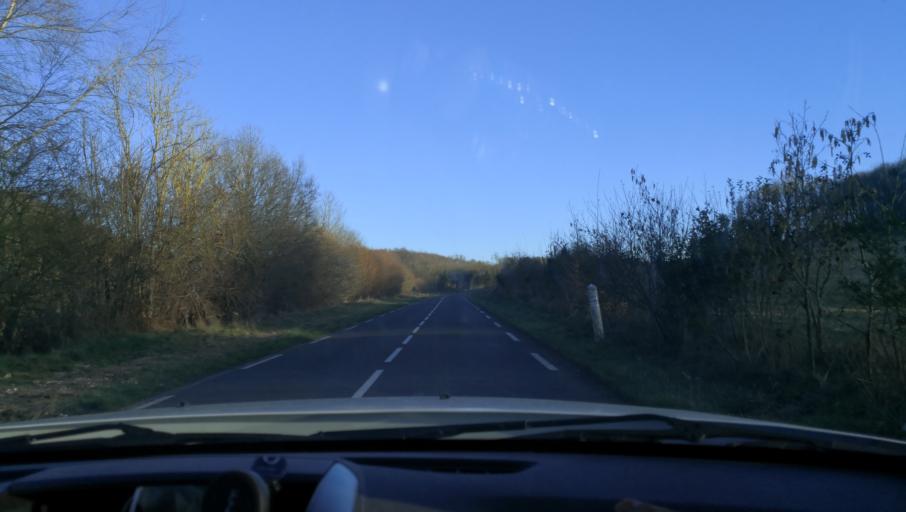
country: FR
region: Haute-Normandie
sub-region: Departement de la Seine-Maritime
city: Saint-Martin-Osmonville
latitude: 49.6235
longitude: 1.3184
